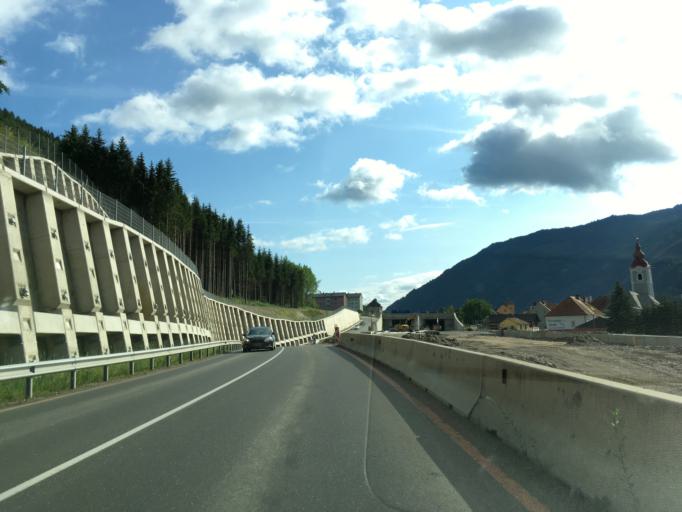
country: AT
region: Styria
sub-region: Politischer Bezirk Murtal
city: Sankt Georgen ob Judenburg
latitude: 47.2012
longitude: 14.4493
